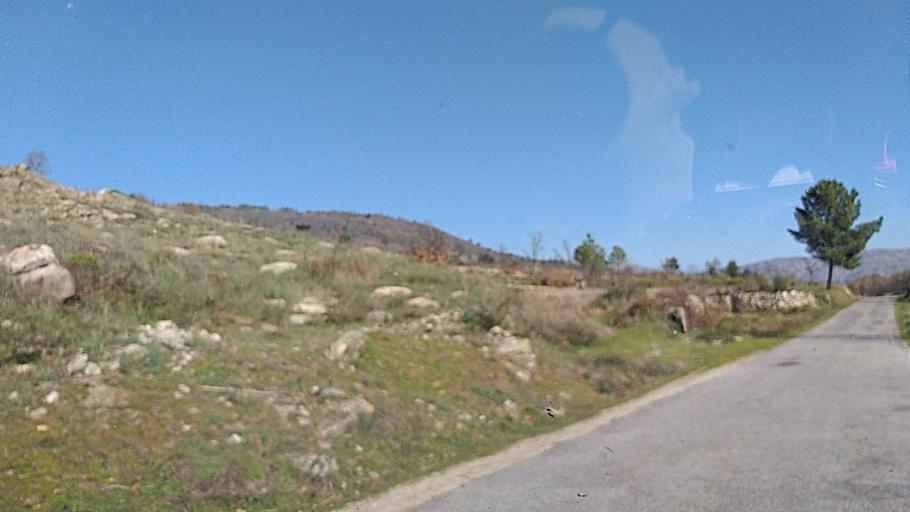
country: PT
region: Guarda
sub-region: Celorico da Beira
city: Celorico da Beira
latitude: 40.6755
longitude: -7.4562
